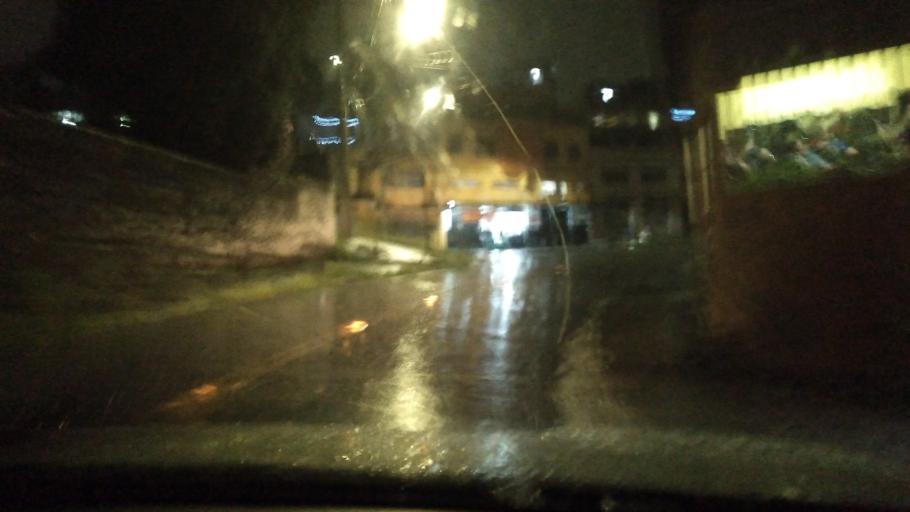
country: BR
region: Minas Gerais
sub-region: Belo Horizonte
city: Belo Horizonte
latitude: -19.8787
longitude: -43.9485
